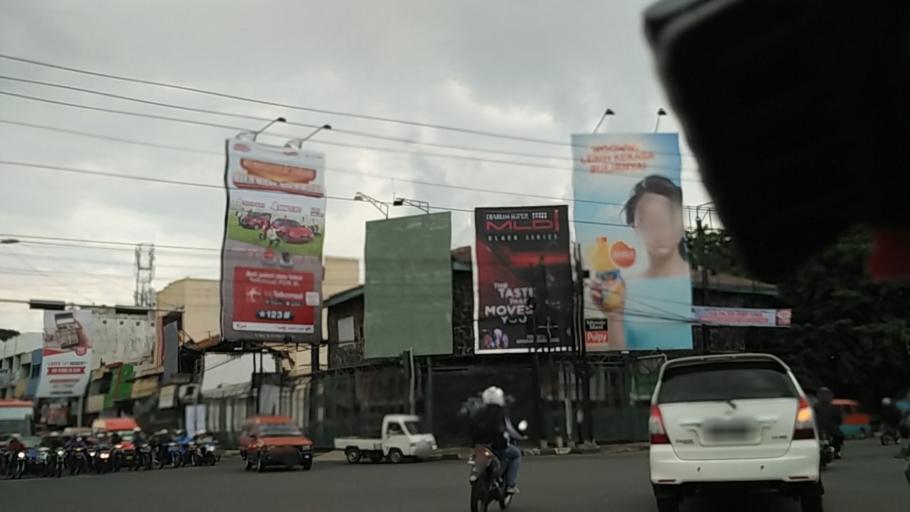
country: ID
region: Central Java
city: Semarang
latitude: -7.0047
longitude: 110.4321
